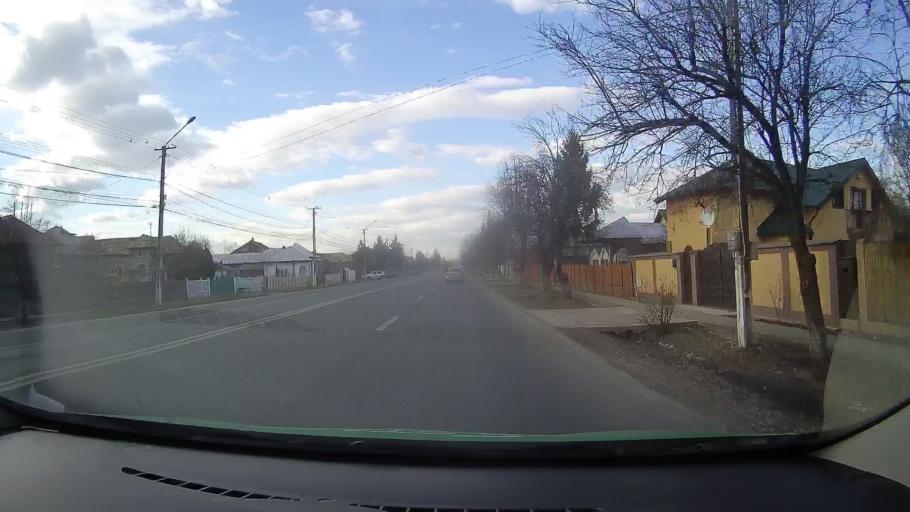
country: RO
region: Dambovita
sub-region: Comuna Ulmi
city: Ulmi
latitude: 44.8961
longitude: 25.5007
